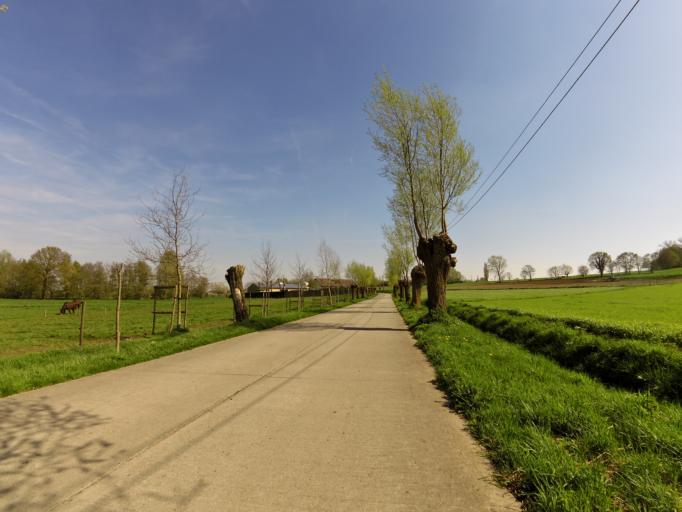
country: BE
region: Flanders
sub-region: Provincie West-Vlaanderen
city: Koekelare
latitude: 51.0849
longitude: 2.9938
